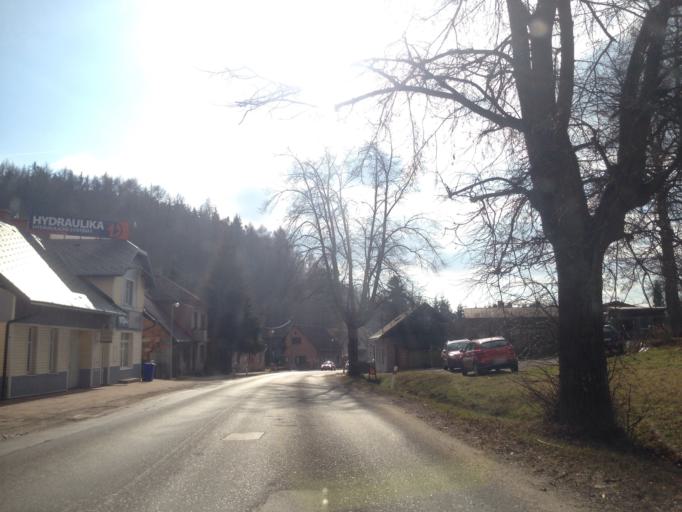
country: CZ
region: Kralovehradecky
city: Nova Paka
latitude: 50.4990
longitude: 15.5272
